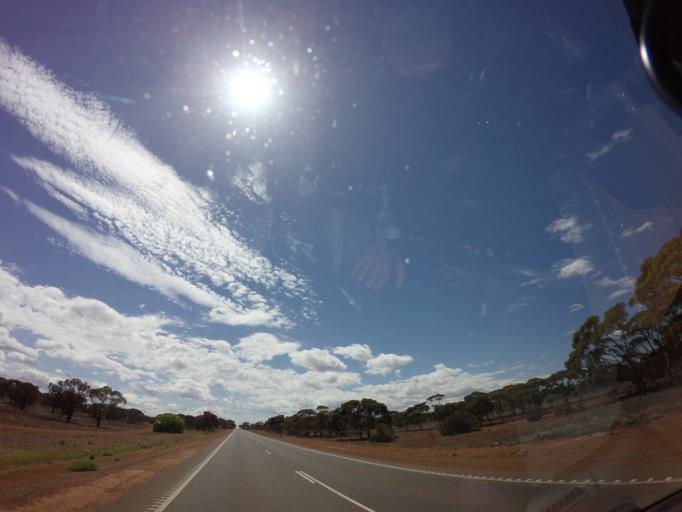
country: AU
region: Western Australia
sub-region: Kalgoorlie/Boulder
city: Boulder
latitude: -30.9546
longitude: 121.1480
